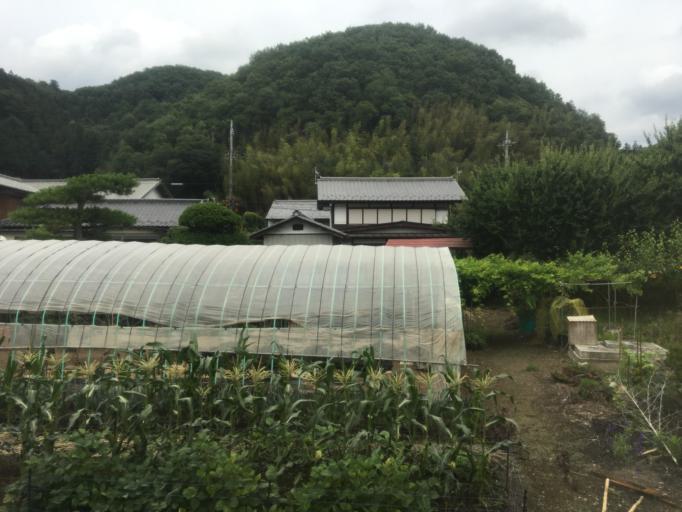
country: JP
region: Gunma
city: Tomioka
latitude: 36.2372
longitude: 138.8123
